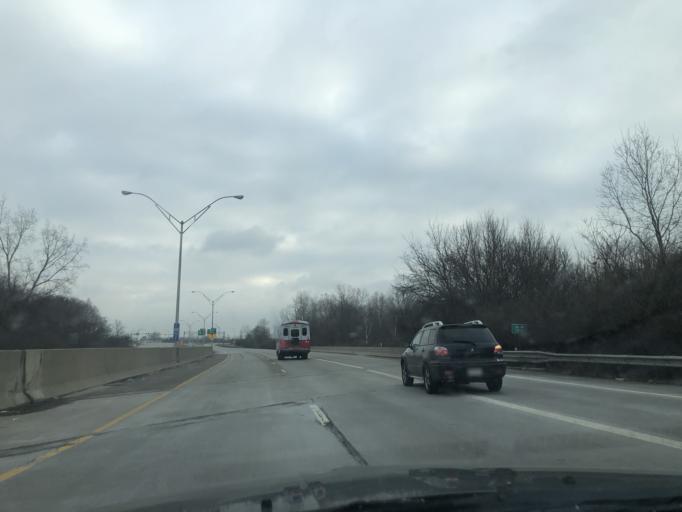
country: US
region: Ohio
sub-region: Franklin County
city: Obetz
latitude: 39.9184
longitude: -82.9266
